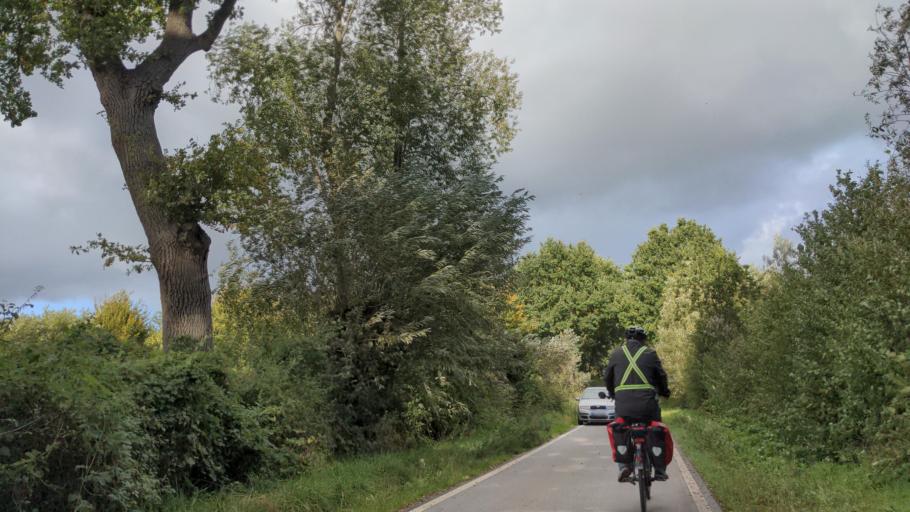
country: DE
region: Schleswig-Holstein
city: Hamberge
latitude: 53.8116
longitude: 10.6138
